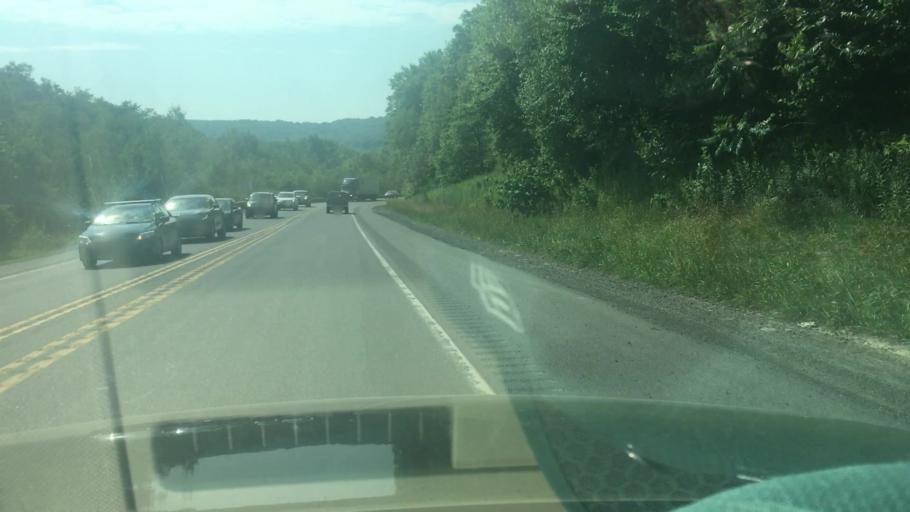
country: US
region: Pennsylvania
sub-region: Northumberland County
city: Mount Carmel
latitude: 40.7971
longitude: -76.4352
